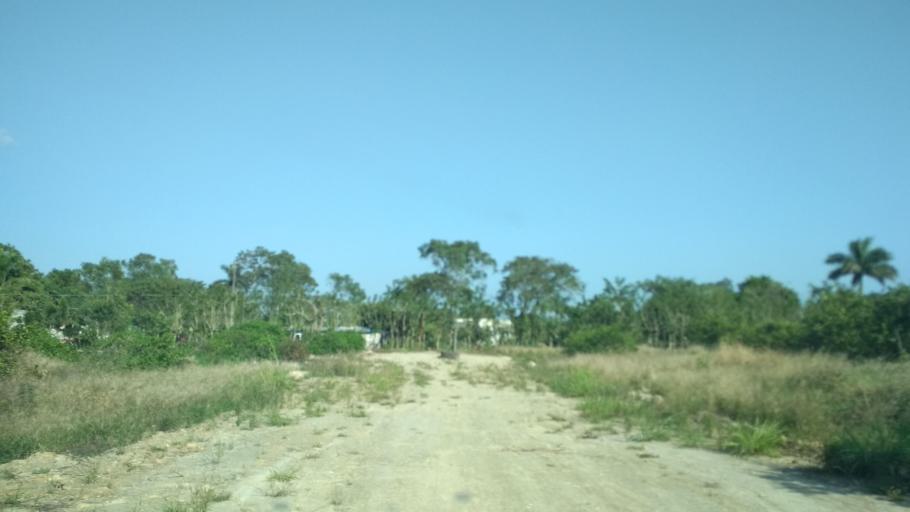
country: MX
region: Veracruz
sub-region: Martinez de la Torre
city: El Progreso
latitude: 20.0865
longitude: -97.0211
